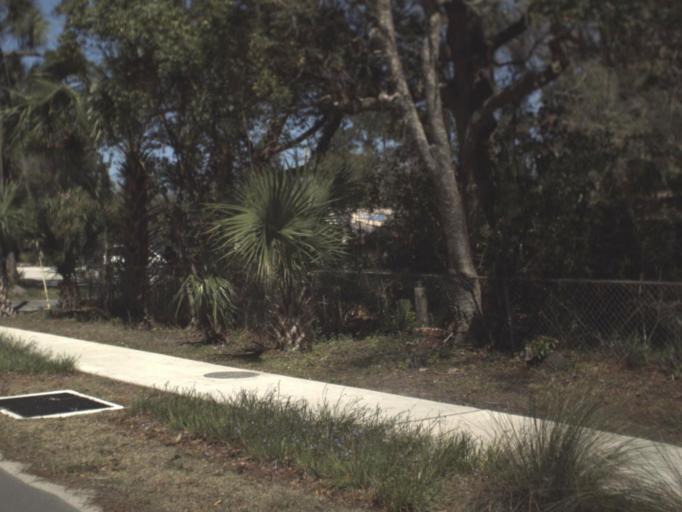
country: US
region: Florida
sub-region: Leon County
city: Woodville
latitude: 30.1573
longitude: -84.2045
